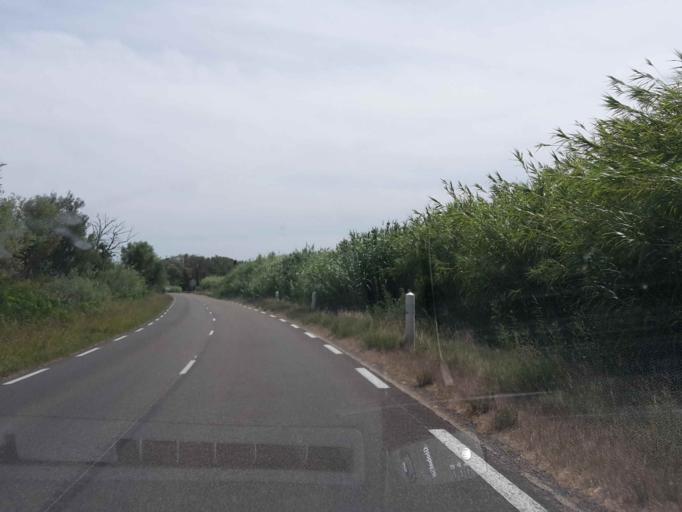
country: FR
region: Provence-Alpes-Cote d'Azur
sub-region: Departement des Bouches-du-Rhone
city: Arles
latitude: 43.6371
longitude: 4.6038
